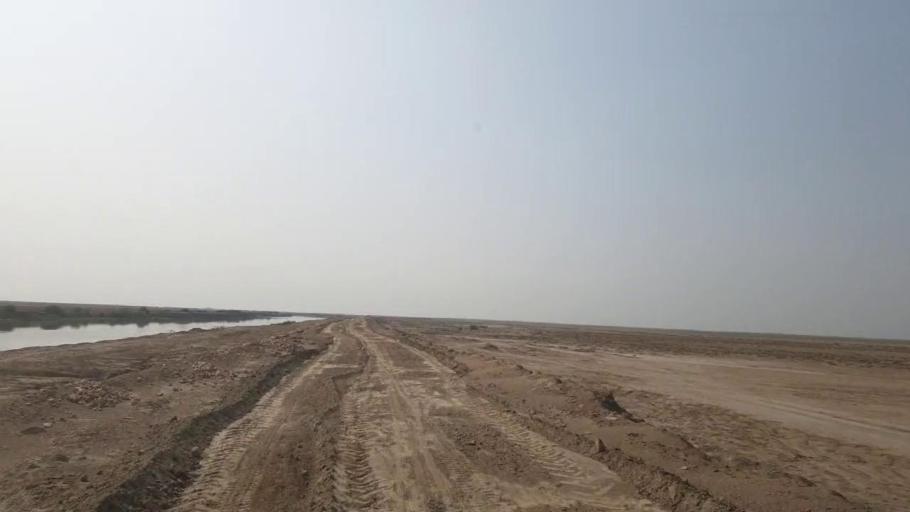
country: PK
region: Sindh
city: Kadhan
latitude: 24.3389
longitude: 68.8535
